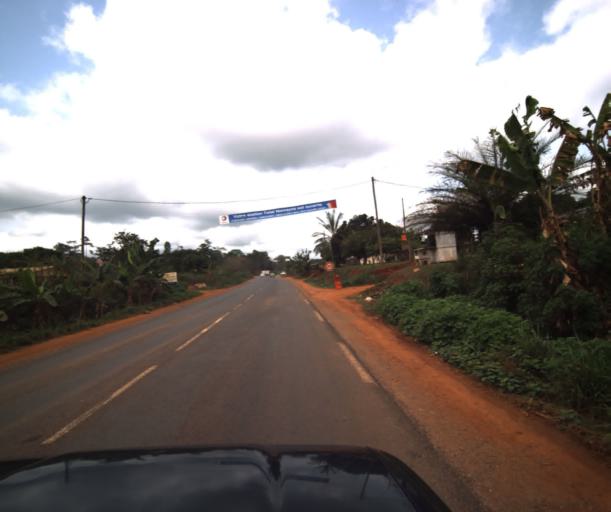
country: CM
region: Centre
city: Mbankomo
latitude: 3.7889
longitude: 11.4326
